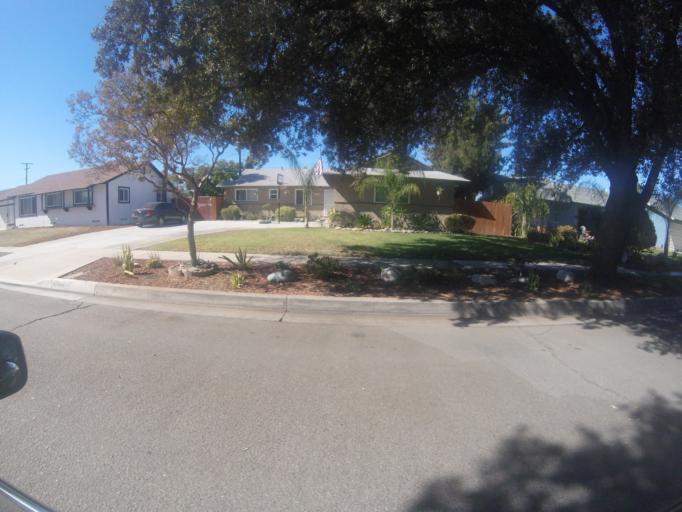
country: US
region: California
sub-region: San Bernardino County
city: Redlands
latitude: 34.0723
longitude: -117.1712
